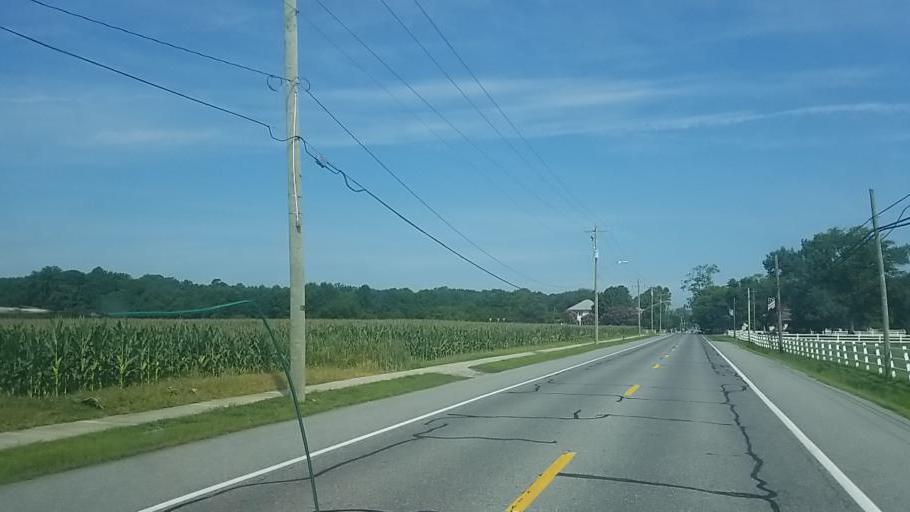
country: US
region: Delaware
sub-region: Sussex County
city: Millsboro
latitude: 38.5429
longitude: -75.2406
